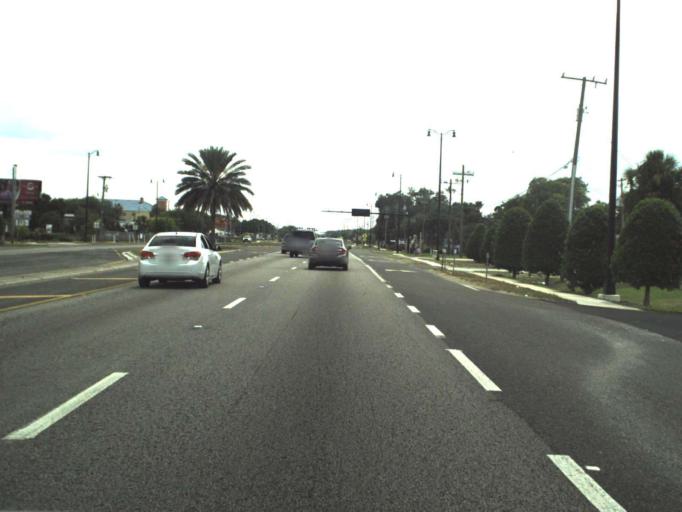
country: US
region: Florida
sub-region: Seminole County
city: Sanford
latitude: 28.7687
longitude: -81.2813
